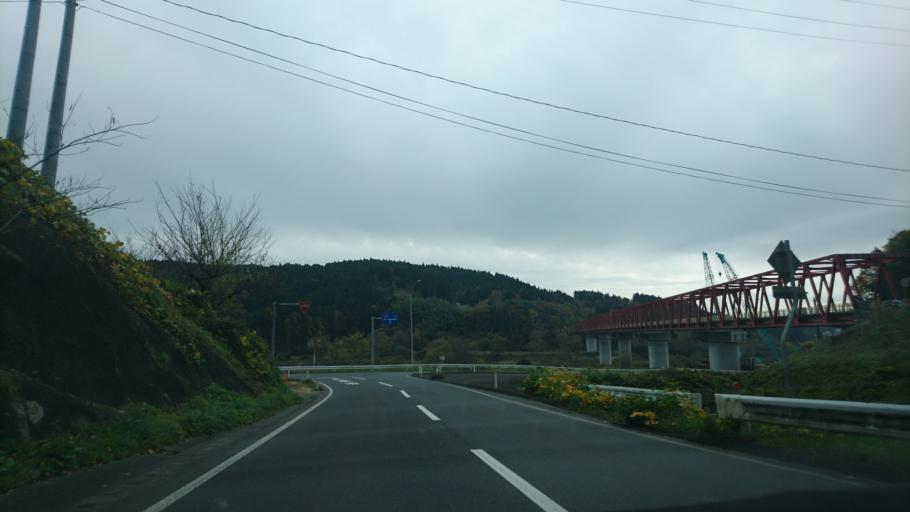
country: JP
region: Iwate
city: Ichinoseki
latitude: 38.9521
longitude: 141.1834
